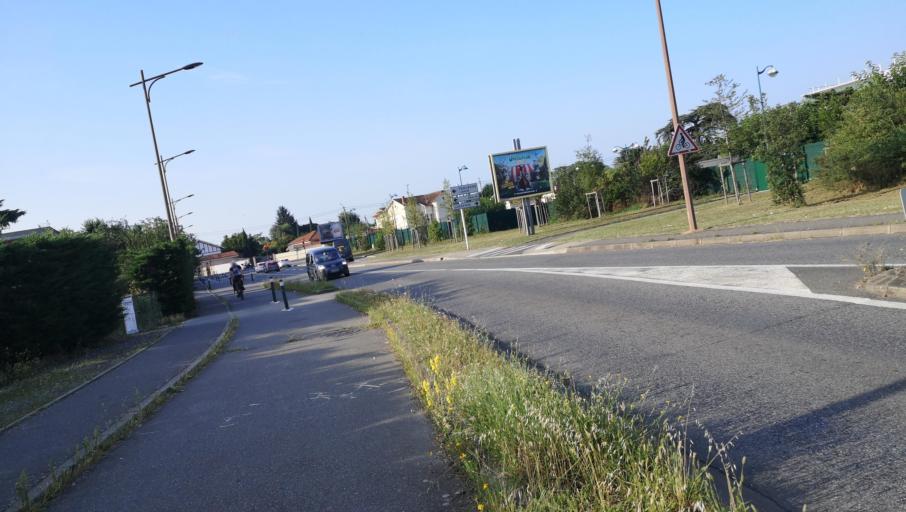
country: FR
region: Midi-Pyrenees
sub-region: Departement de la Haute-Garonne
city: Blagnac
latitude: 43.5946
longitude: 1.3933
